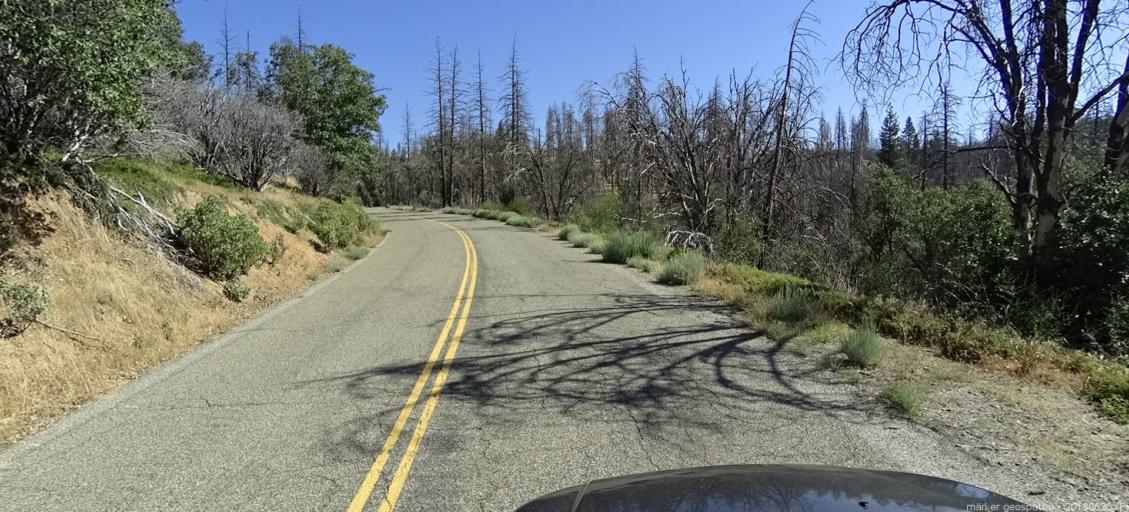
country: US
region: California
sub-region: Fresno County
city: Auberry
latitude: 37.2492
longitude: -119.3468
